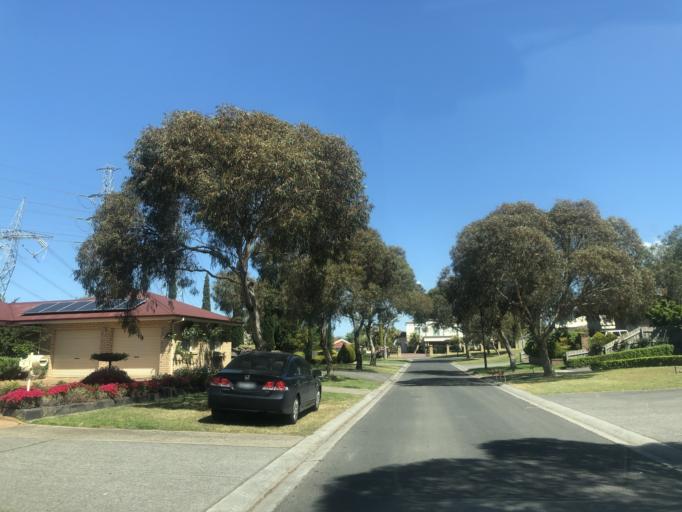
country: AU
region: Victoria
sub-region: Casey
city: Narre Warren North
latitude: -37.9919
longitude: 145.2866
